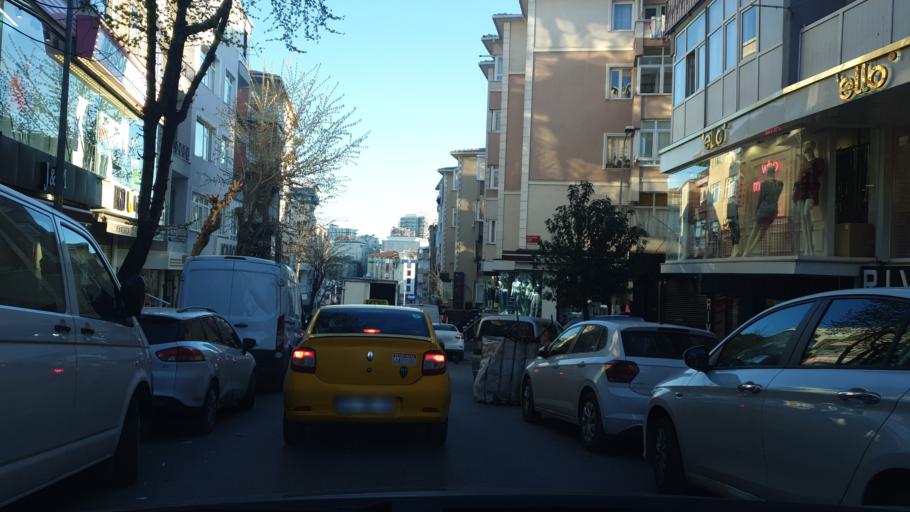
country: TR
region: Istanbul
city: merter keresteciler
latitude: 41.0173
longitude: 28.8759
